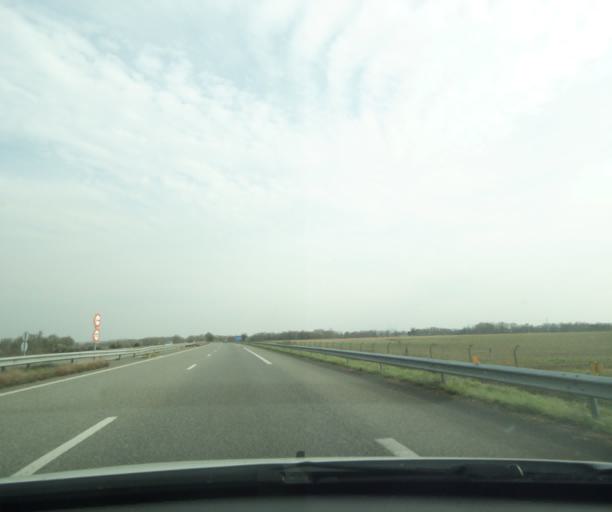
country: FR
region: Aquitaine
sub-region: Departement des Pyrenees-Atlantiques
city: Mont
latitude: 43.4298
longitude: -0.6276
